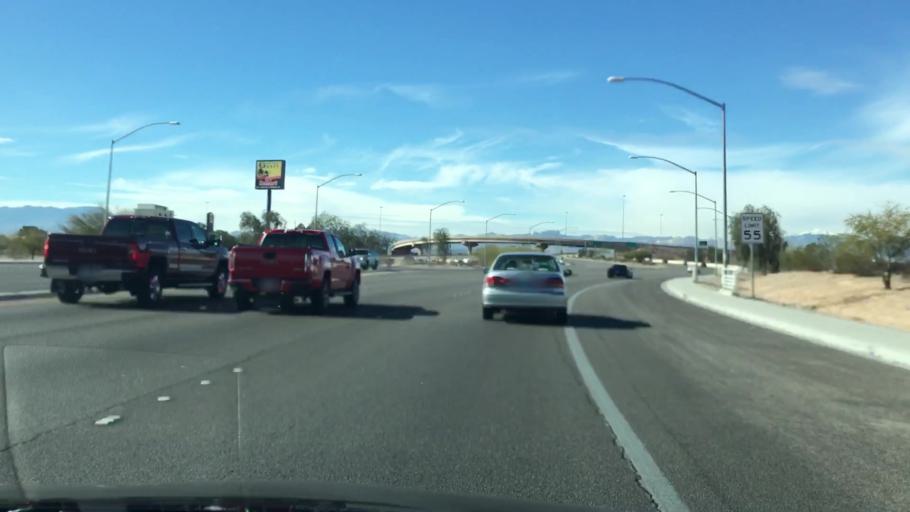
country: US
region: Nevada
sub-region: Clark County
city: Paradise
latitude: 36.0420
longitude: -115.1754
